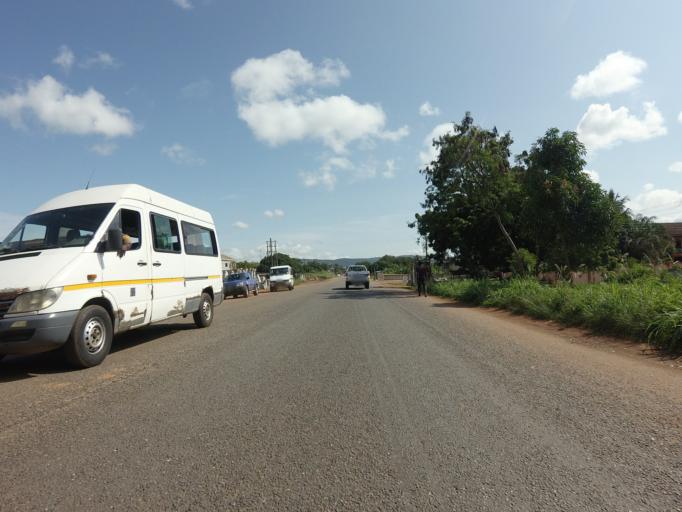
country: GH
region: Eastern
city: Aburi
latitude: 5.8493
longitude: -0.1137
